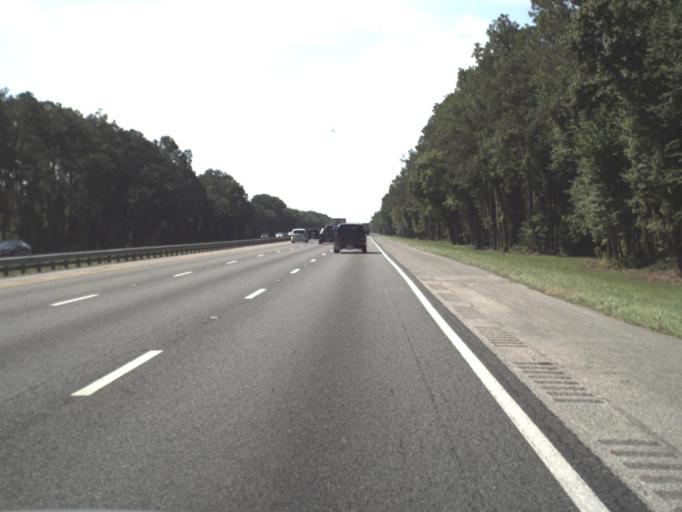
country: US
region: Florida
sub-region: Saint Johns County
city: Fruit Cove
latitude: 30.0331
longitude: -81.4904
